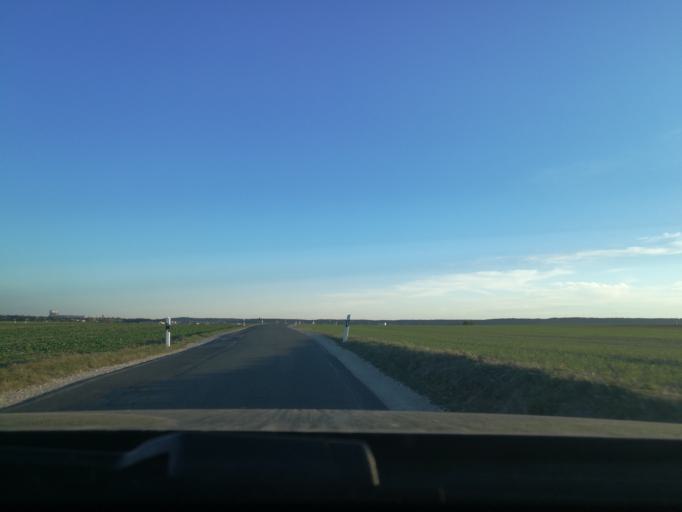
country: DE
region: Bavaria
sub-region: Regierungsbezirk Mittelfranken
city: Obermichelbach
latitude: 49.5011
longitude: 10.9346
